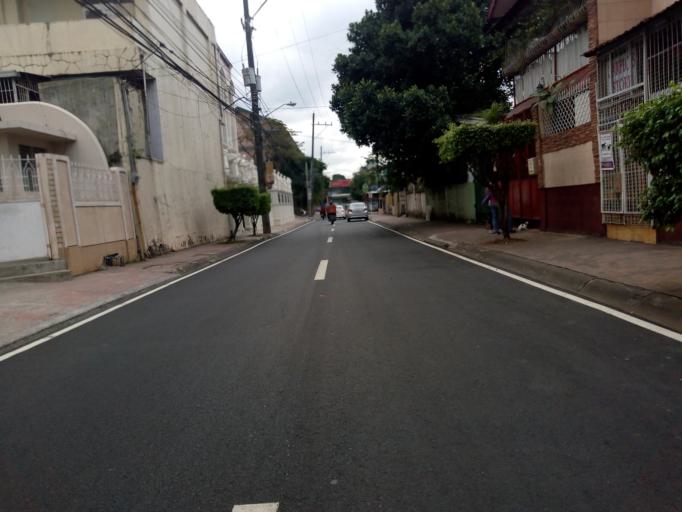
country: PH
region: Calabarzon
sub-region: Province of Rizal
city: Antipolo
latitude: 14.6397
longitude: 121.1200
